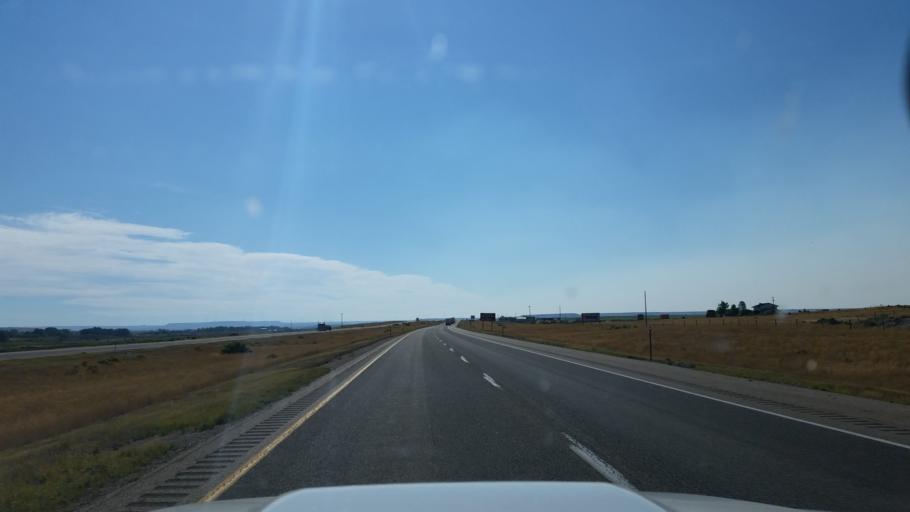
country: US
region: Wyoming
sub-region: Uinta County
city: Lyman
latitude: 41.3723
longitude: -110.2591
